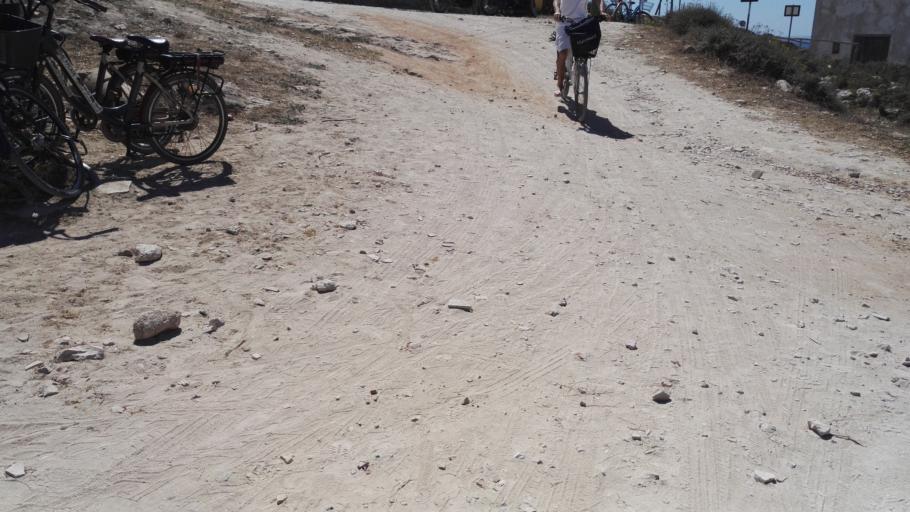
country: IT
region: Sicily
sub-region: Trapani
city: Favignana
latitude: 37.9097
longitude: 12.3616
